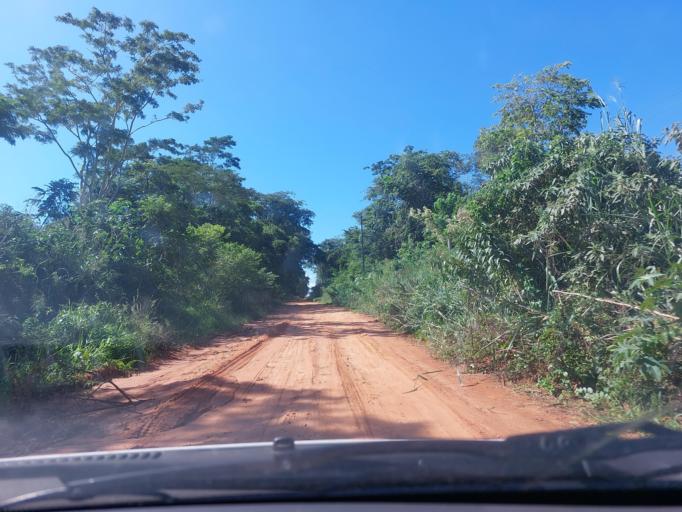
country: PY
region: San Pedro
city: Itacurubi del Rosario
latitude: -24.5414
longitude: -56.5831
